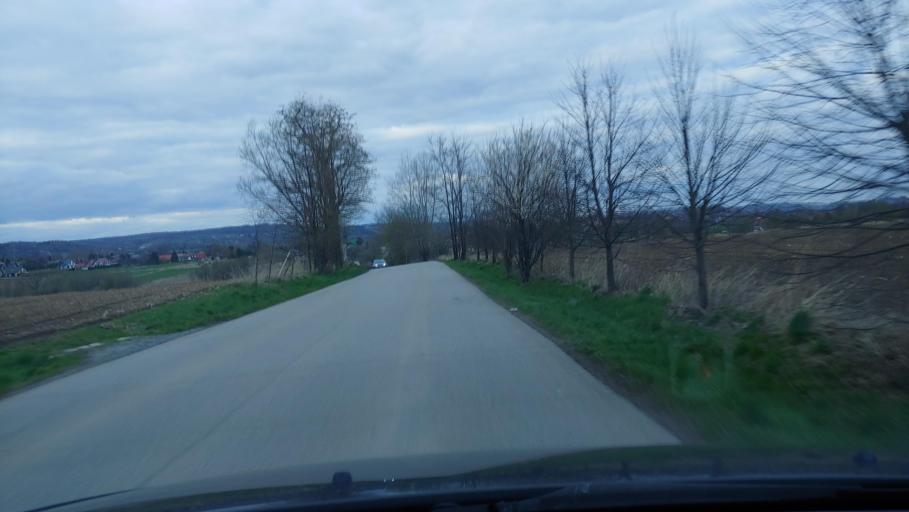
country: PL
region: Lesser Poland Voivodeship
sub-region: Powiat krakowski
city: Rudawa
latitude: 50.1298
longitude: 19.7304
